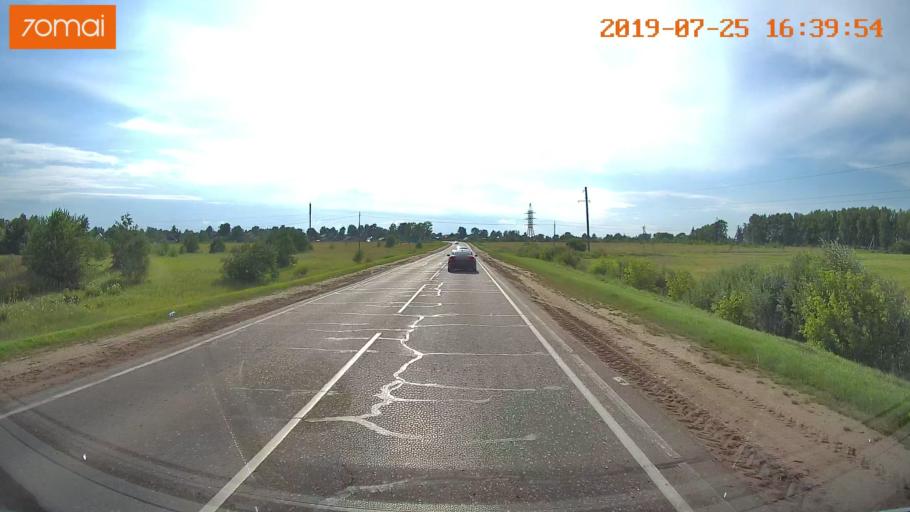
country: RU
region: Ivanovo
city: Privolzhsk
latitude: 57.3866
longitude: 41.3170
